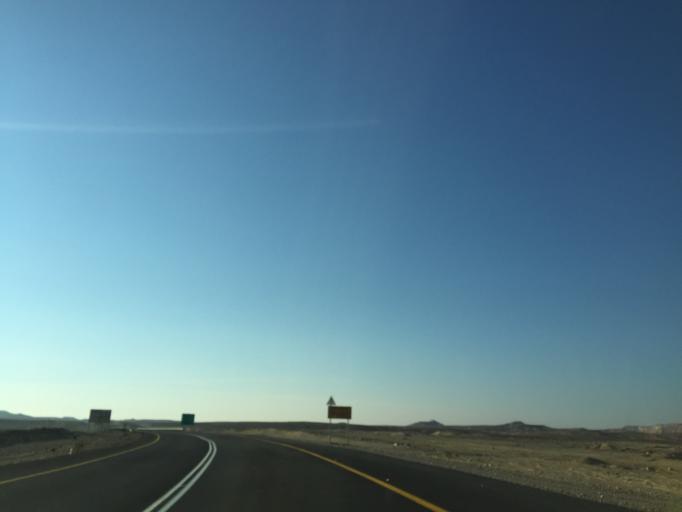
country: IL
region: Southern District
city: Mitzpe Ramon
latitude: 30.2757
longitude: 35.0204
